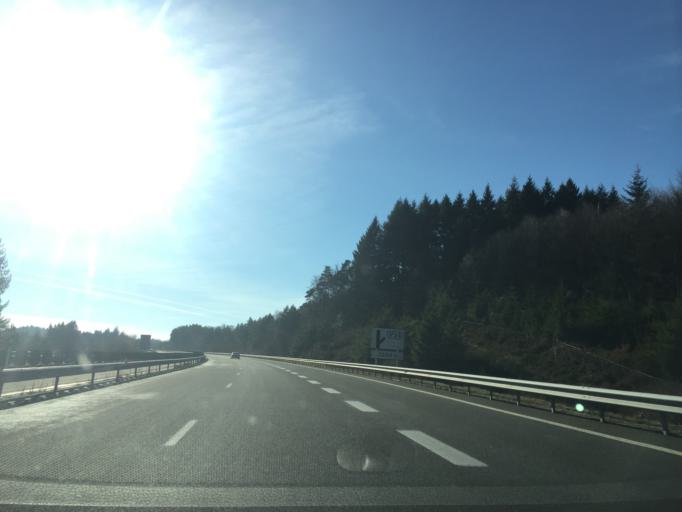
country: FR
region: Limousin
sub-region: Departement de la Correze
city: Egletons
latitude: 45.4285
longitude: 2.0416
